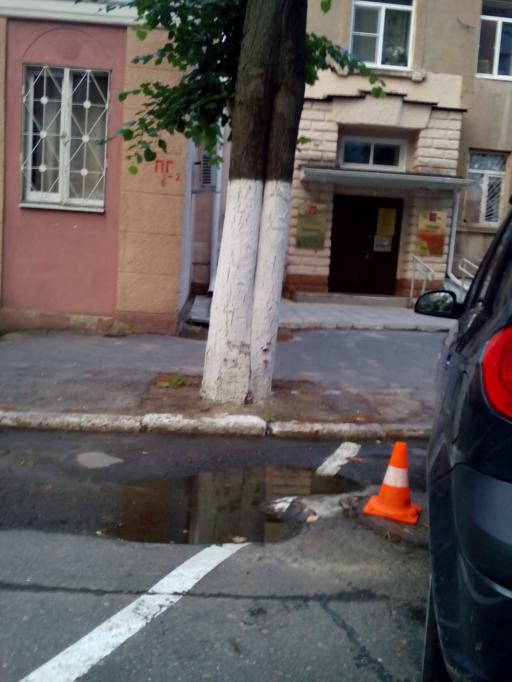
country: RU
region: Voronezj
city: Voronezh
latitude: 51.6587
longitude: 39.2064
